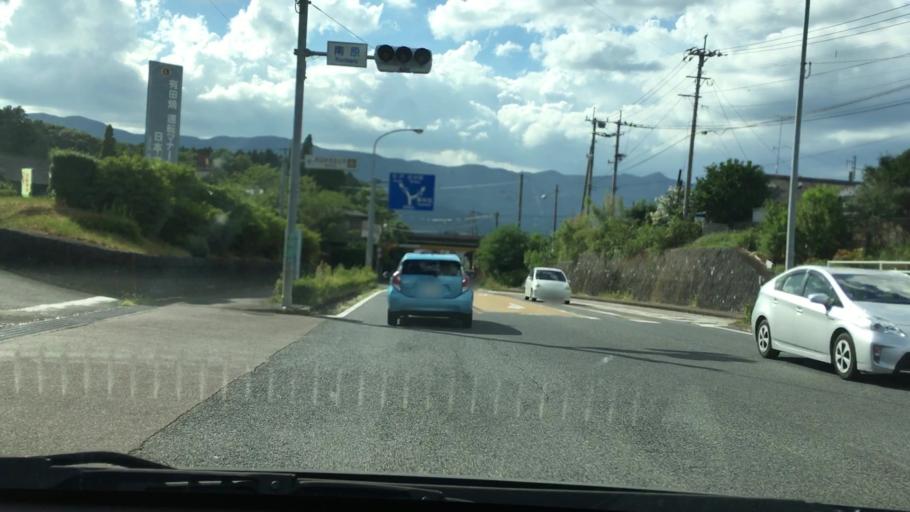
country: JP
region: Saga Prefecture
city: Imaricho-ko
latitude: 33.1875
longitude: 129.8656
